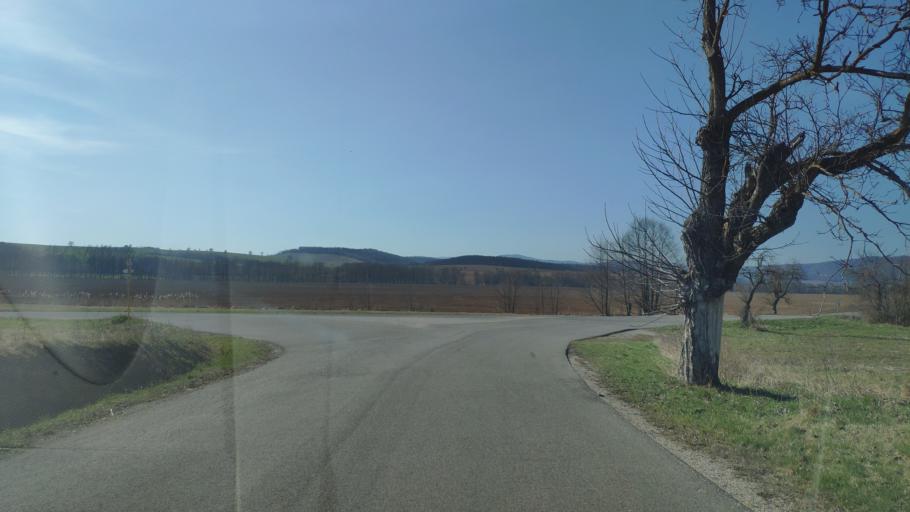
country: SK
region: Banskobystricky
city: Revuca
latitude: 48.5474
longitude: 20.3036
